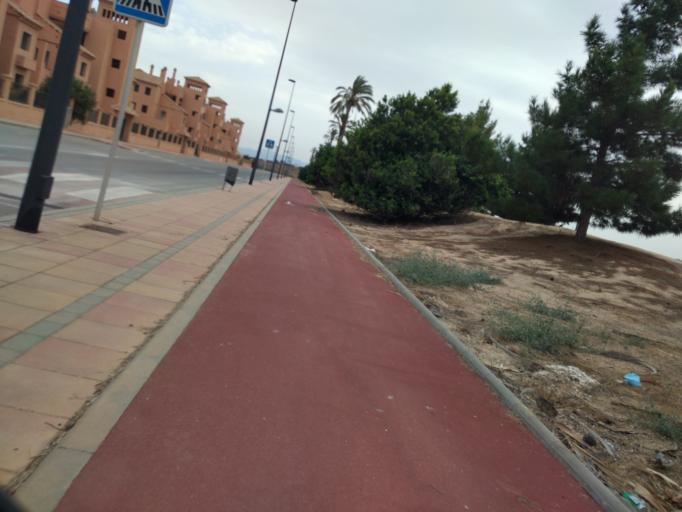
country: ES
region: Murcia
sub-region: Murcia
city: Los Alcazares
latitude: 37.7236
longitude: -0.8700
